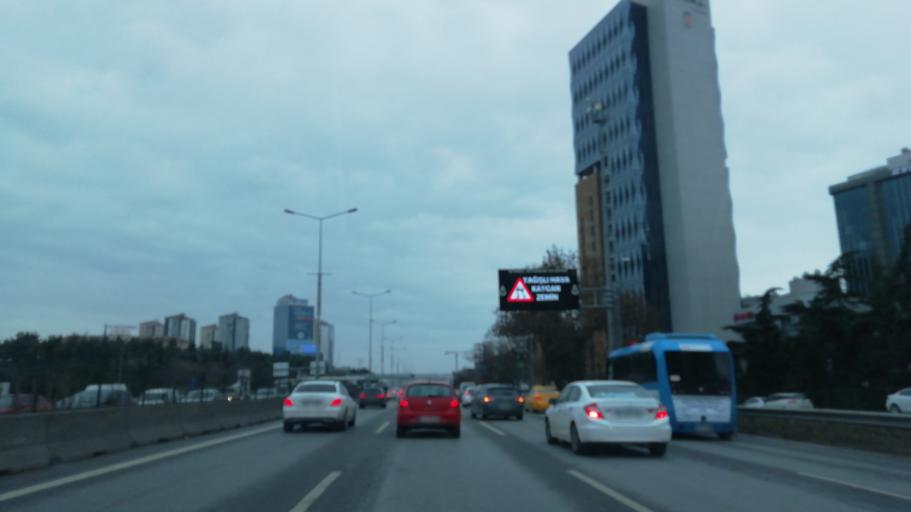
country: TR
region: Istanbul
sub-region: Atasehir
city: Atasehir
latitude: 40.9726
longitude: 29.1004
